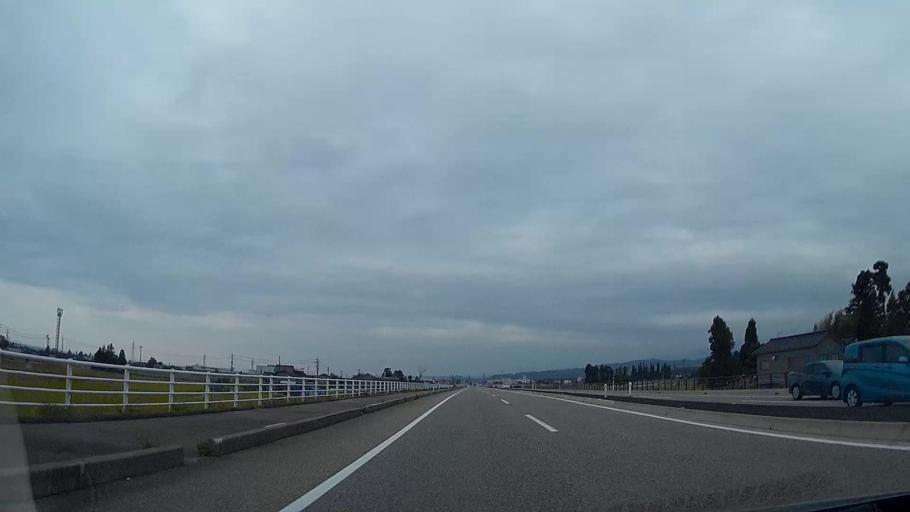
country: JP
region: Toyama
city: Uozu
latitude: 36.7700
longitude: 137.3821
